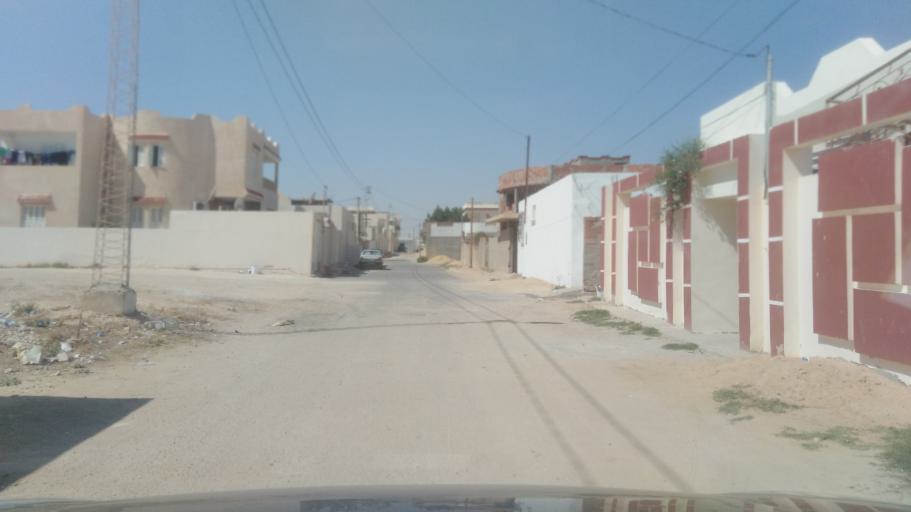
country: TN
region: Qabis
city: Gabes
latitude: 33.9566
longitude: 10.0144
